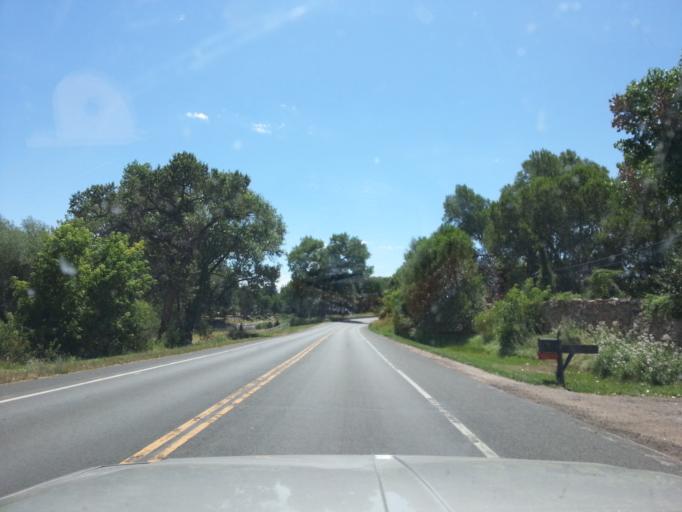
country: US
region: Colorado
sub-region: Larimer County
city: Loveland
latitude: 40.4158
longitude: -105.1724
